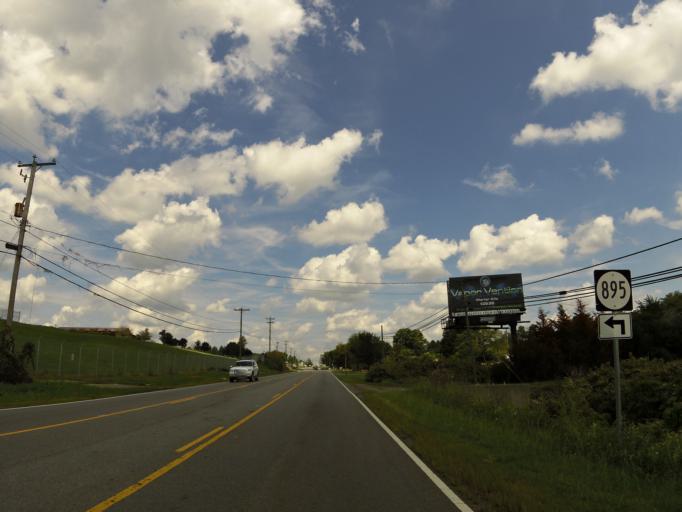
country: US
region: Virginia
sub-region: Washington County
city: Abingdon
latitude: 36.6916
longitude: -82.0233
